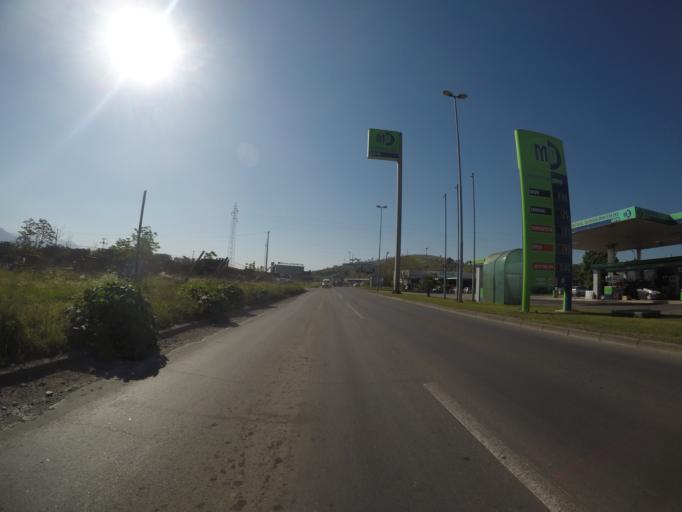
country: ME
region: Podgorica
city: Podgorica
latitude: 42.4287
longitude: 19.2325
